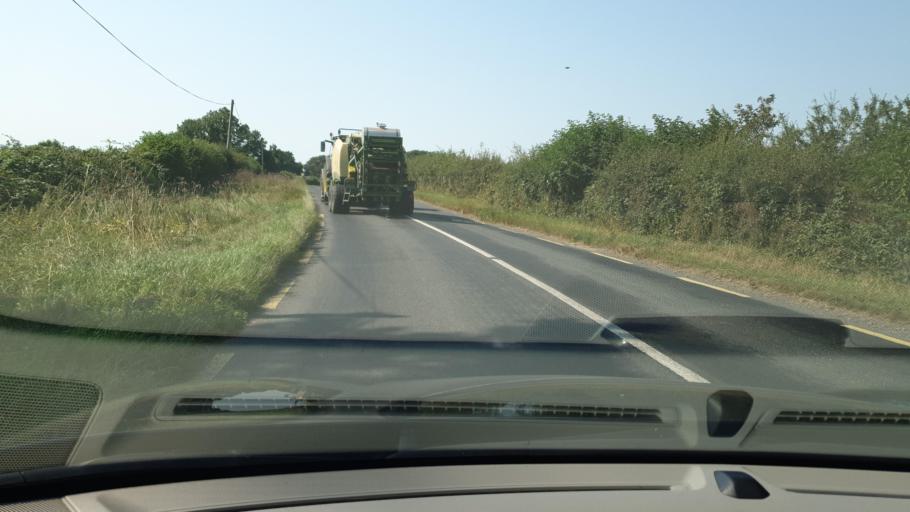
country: IE
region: Leinster
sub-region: An Mhi
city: Athboy
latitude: 53.5901
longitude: -6.8578
